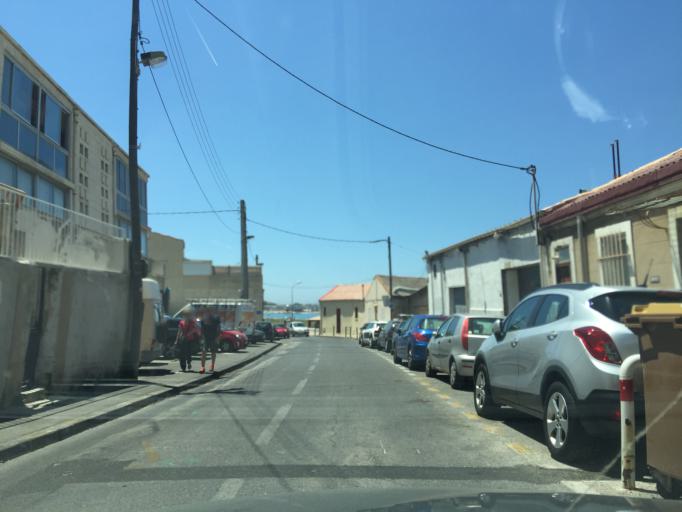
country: FR
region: Provence-Alpes-Cote d'Azur
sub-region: Departement des Bouches-du-Rhone
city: Marseille 08
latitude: 43.2503
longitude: 5.3762
